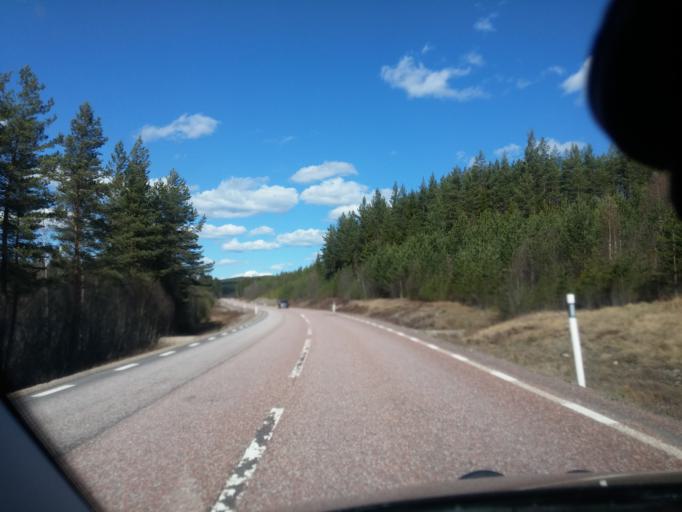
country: SE
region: Dalarna
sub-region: Faluns Kommun
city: Svardsjo
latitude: 60.7390
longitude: 15.7687
